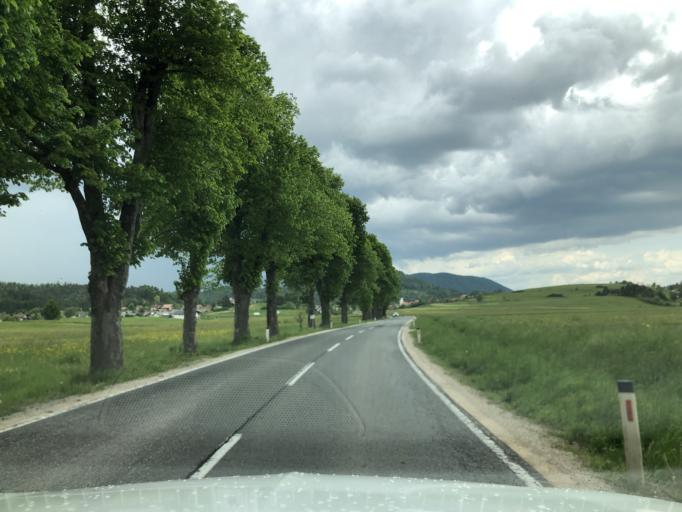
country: SI
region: Cerknica
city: Rakek
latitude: 45.8154
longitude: 14.3035
